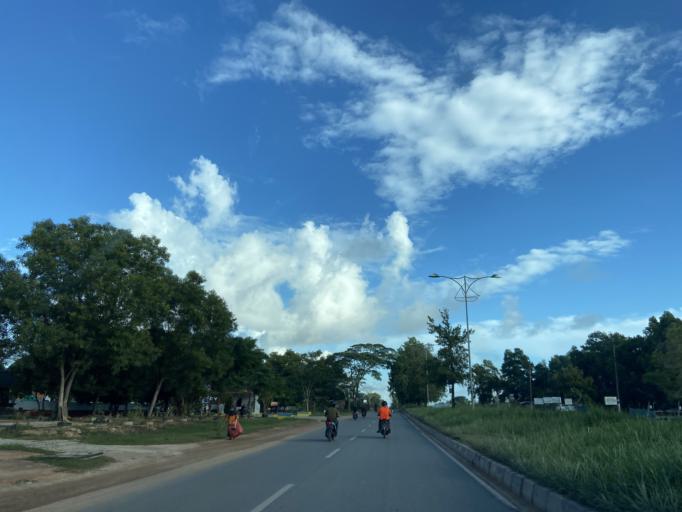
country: SG
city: Singapore
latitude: 1.0327
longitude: 104.0009
